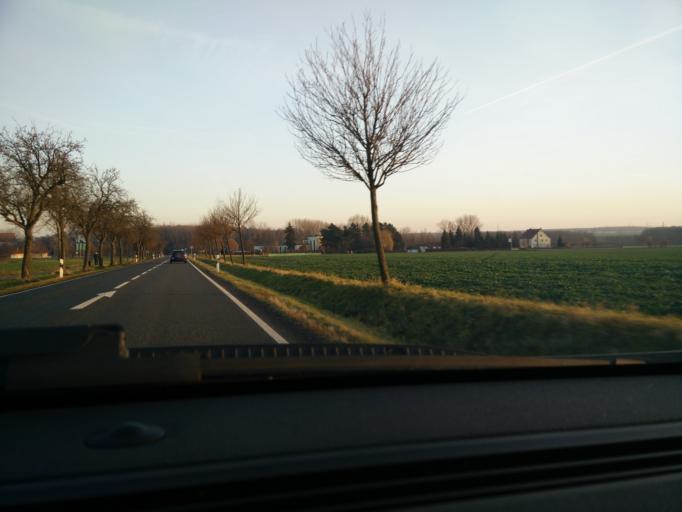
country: DE
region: Saxony
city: Kitzscher
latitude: 51.1655
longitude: 12.5398
